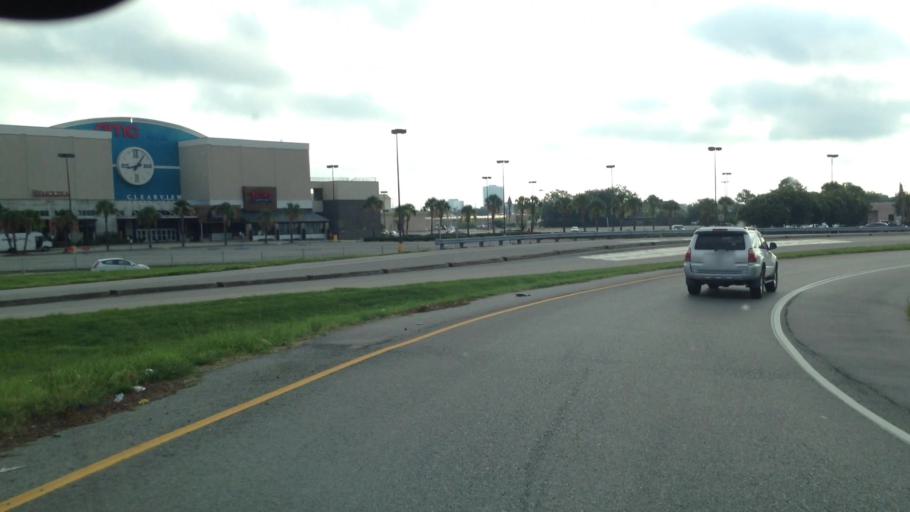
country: US
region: Louisiana
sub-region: Jefferson Parish
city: Metairie Terrace
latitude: 30.0007
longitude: -90.1841
